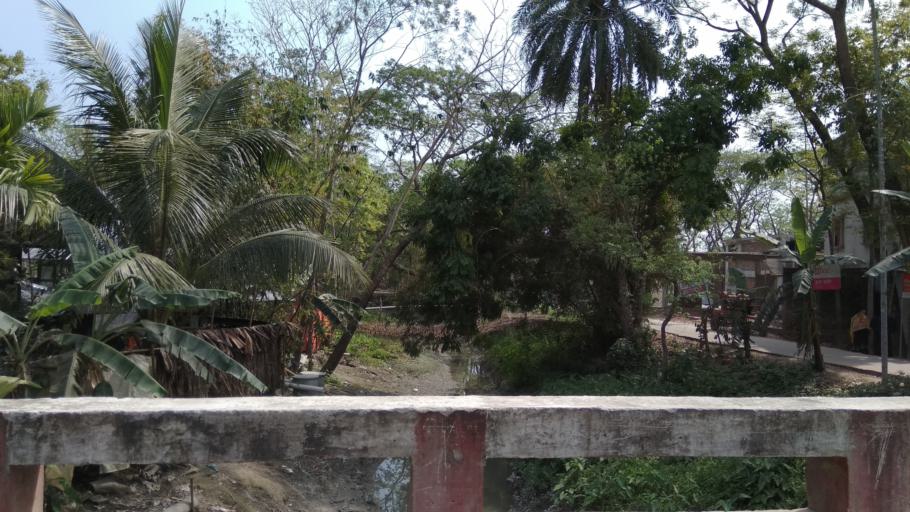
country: BD
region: Barisal
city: Gaurnadi
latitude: 22.9924
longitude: 90.3705
